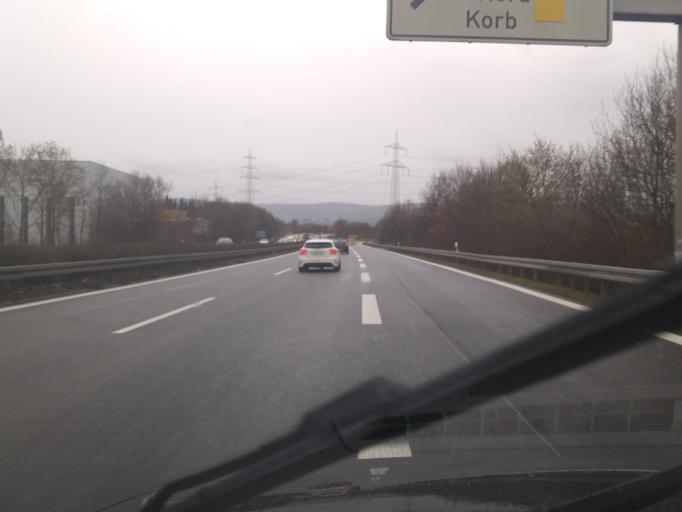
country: DE
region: Baden-Wuerttemberg
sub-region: Regierungsbezirk Stuttgart
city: Korb
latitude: 48.8452
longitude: 9.3457
